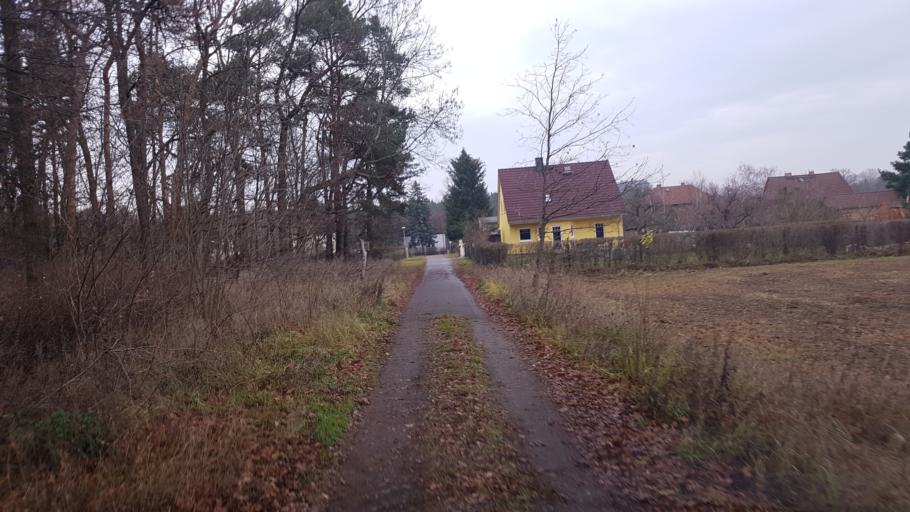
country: DE
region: Brandenburg
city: Sallgast
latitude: 51.5587
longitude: 13.8769
